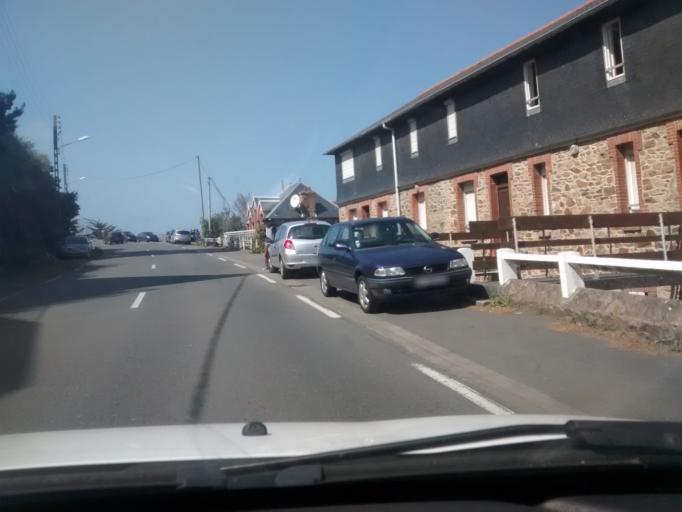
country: FR
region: Brittany
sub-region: Departement des Cotes-d'Armor
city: Perros-Guirec
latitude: 48.8186
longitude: -3.4355
